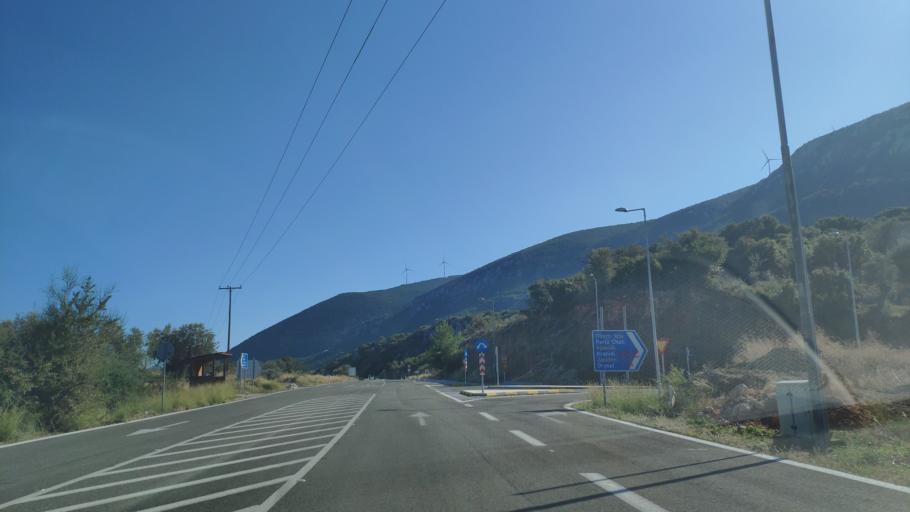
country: GR
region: Peloponnese
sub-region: Nomos Argolidos
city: Palaia Epidavros
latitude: 37.5663
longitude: 23.2526
